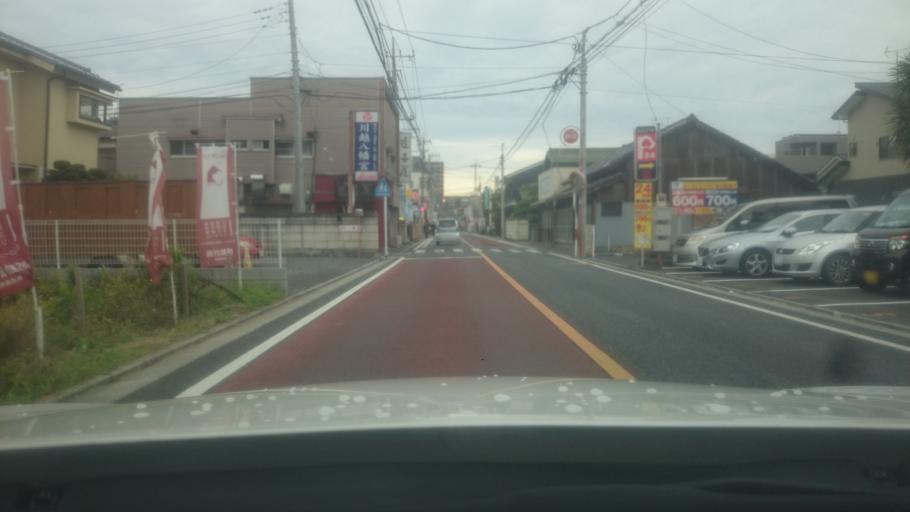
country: JP
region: Saitama
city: Kawagoe
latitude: 35.9111
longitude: 139.4860
